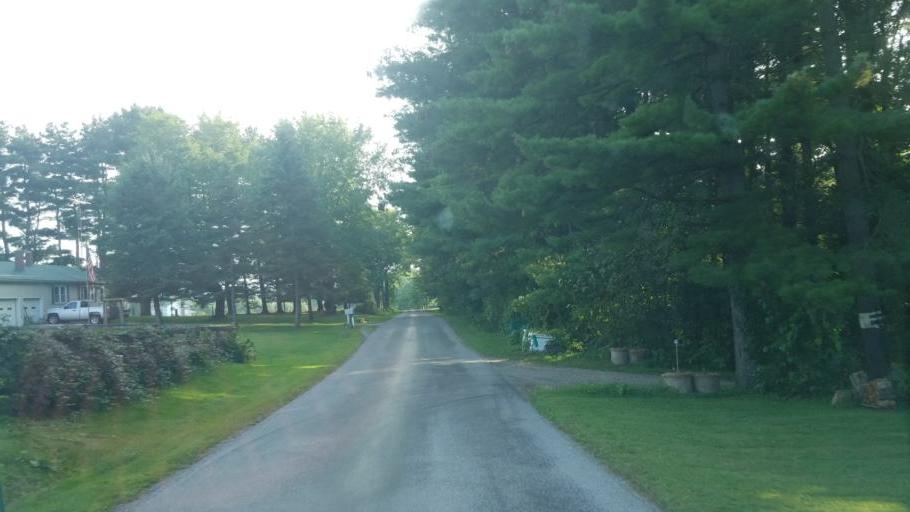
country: US
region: Ohio
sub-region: Wayne County
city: Wooster
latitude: 40.8794
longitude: -82.0220
